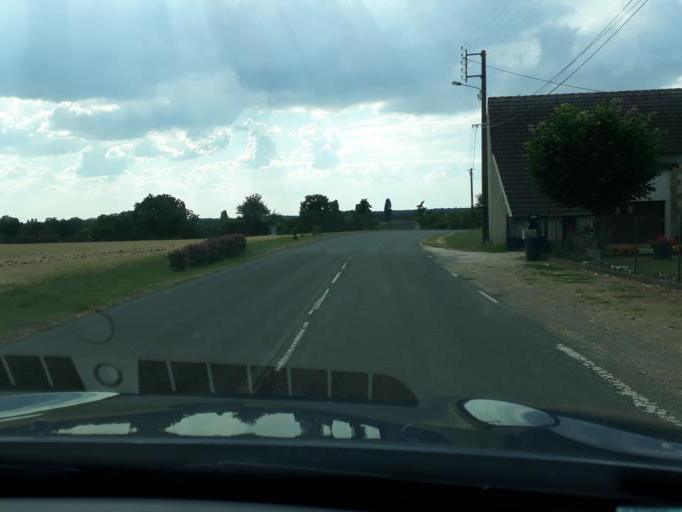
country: FR
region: Centre
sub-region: Departement du Cher
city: Baugy
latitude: 47.0938
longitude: 2.6803
